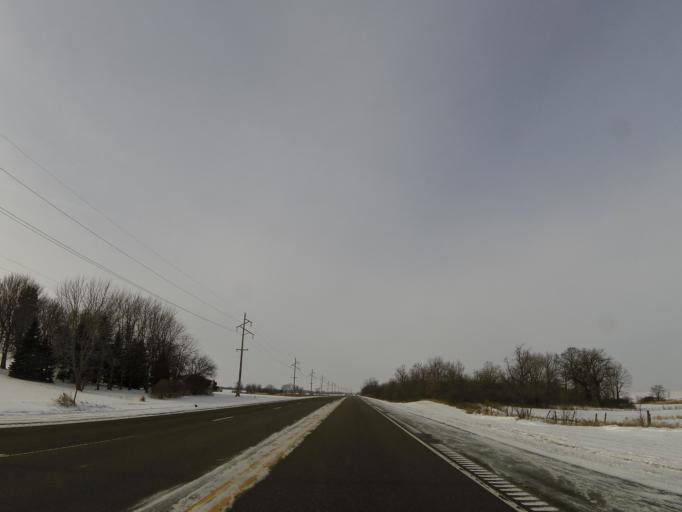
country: US
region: Minnesota
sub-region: Carver County
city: Mayer
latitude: 44.9056
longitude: -93.8501
